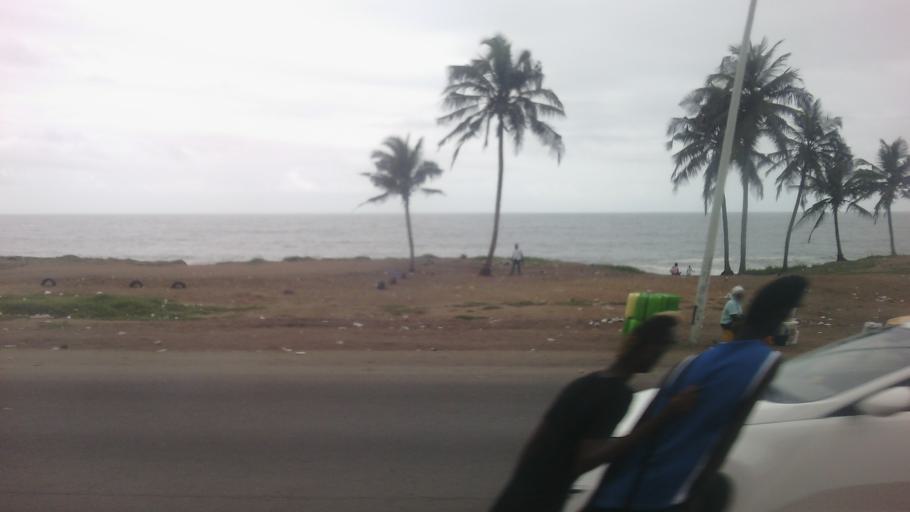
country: CI
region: Lagunes
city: Bingerville
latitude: 5.2412
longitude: -3.9078
